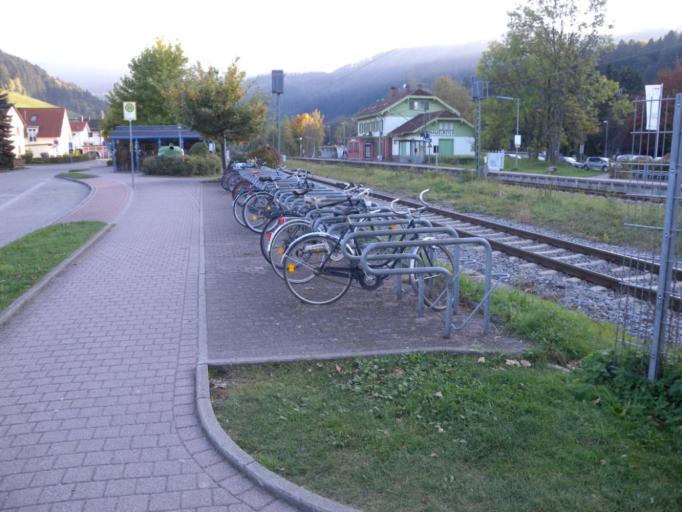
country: DE
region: Baden-Wuerttemberg
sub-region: Freiburg Region
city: Buchenbach
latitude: 47.9594
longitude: 7.9915
